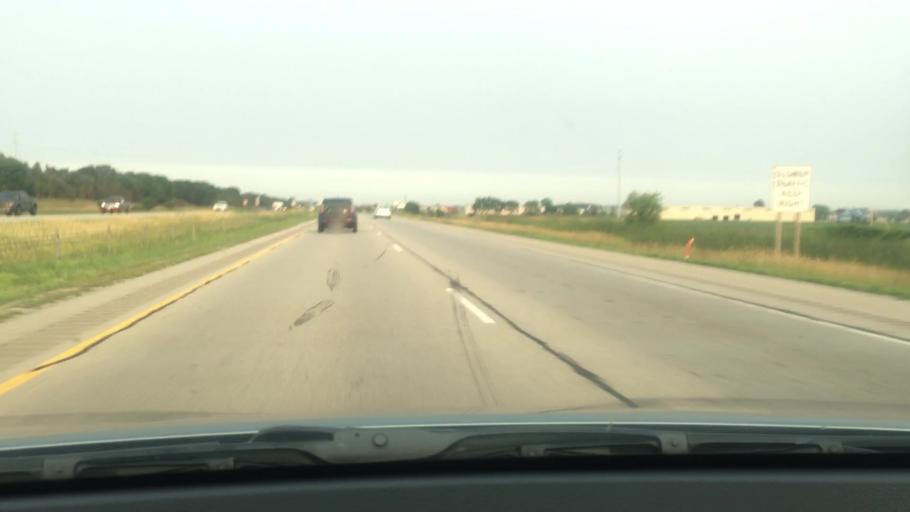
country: US
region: Wisconsin
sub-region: Outagamie County
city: Kimberly
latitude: 44.2981
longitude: -88.3386
